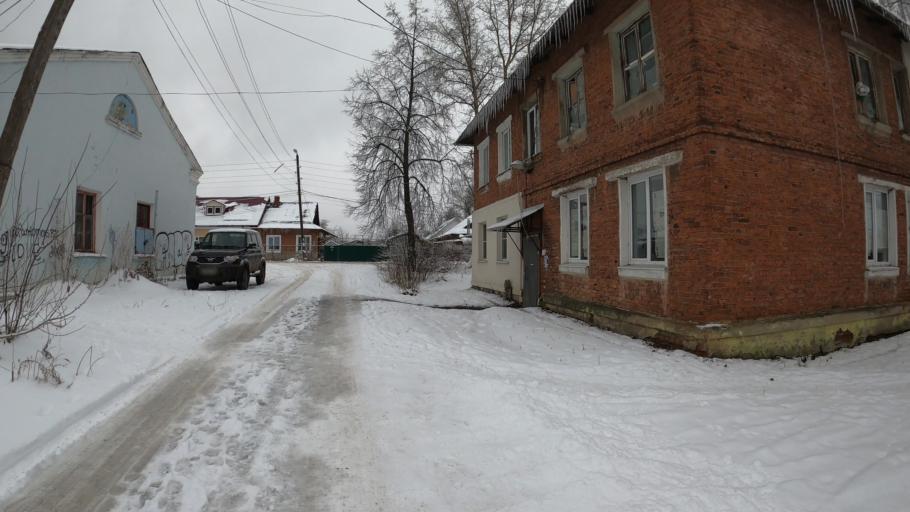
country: RU
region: Jaroslavl
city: Pereslavl'-Zalesskiy
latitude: 56.7499
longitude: 38.8644
